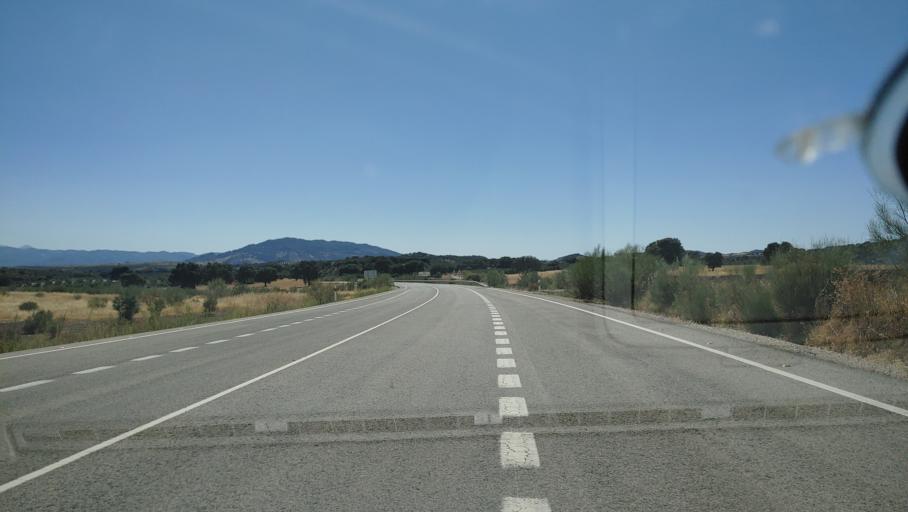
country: ES
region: Andalusia
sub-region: Provincia de Jaen
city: Genave
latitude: 38.4703
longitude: -2.7583
